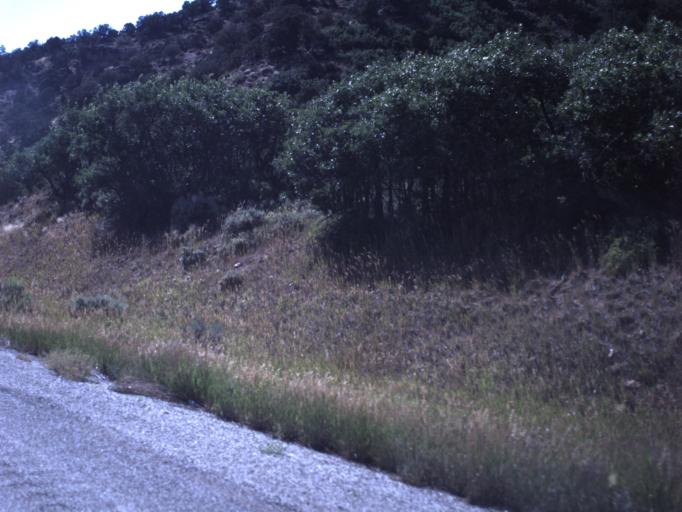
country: US
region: Utah
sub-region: Carbon County
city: Helper
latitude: 40.1958
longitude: -110.9309
